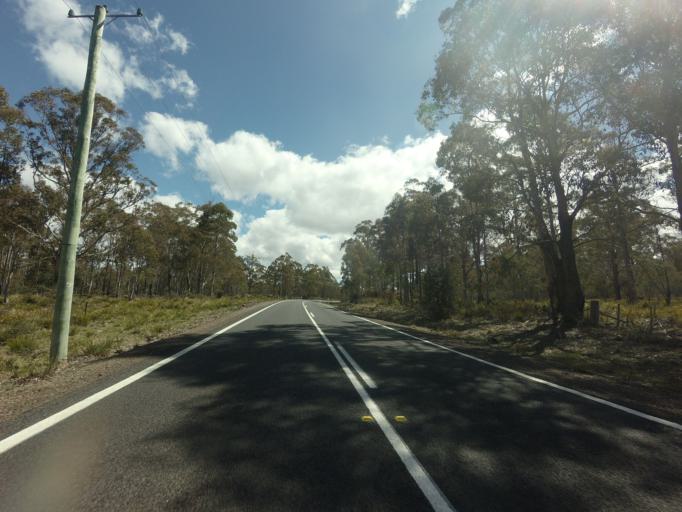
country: AU
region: Tasmania
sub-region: Northern Midlands
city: Evandale
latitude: -42.0346
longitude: 147.8179
